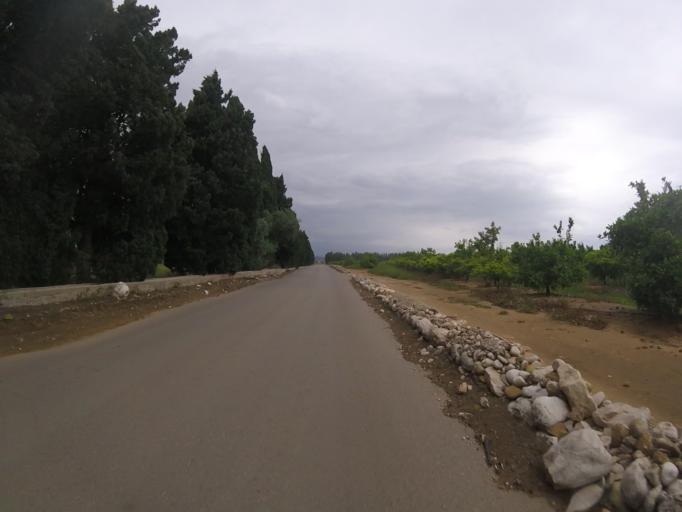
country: ES
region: Valencia
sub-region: Provincia de Castello
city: Alcoceber
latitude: 40.2097
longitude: 0.2523
